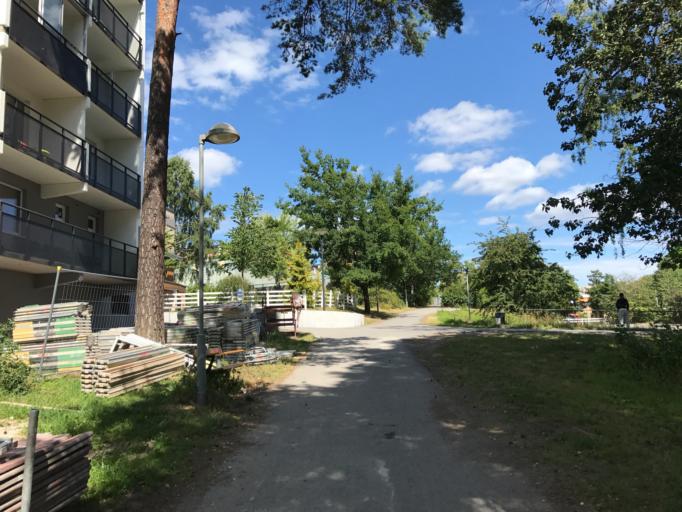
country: SE
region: Stockholm
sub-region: Stockholms Kommun
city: Kista
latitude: 59.4061
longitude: 17.9330
